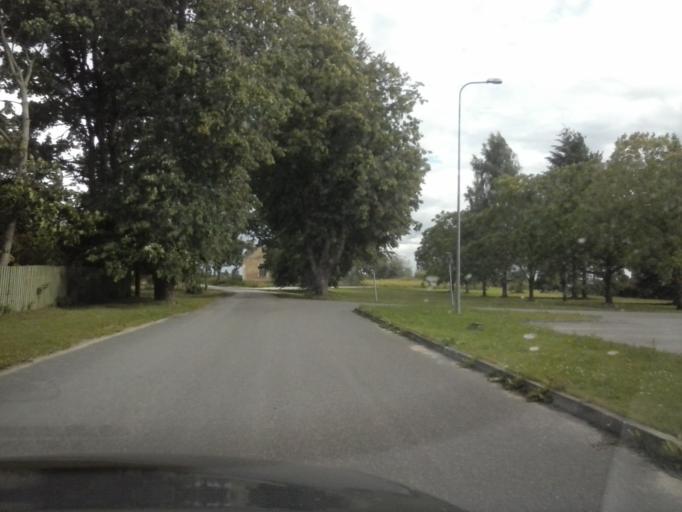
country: EE
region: Jaervamaa
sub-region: Koeru vald
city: Koeru
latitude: 58.9627
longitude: 26.0284
